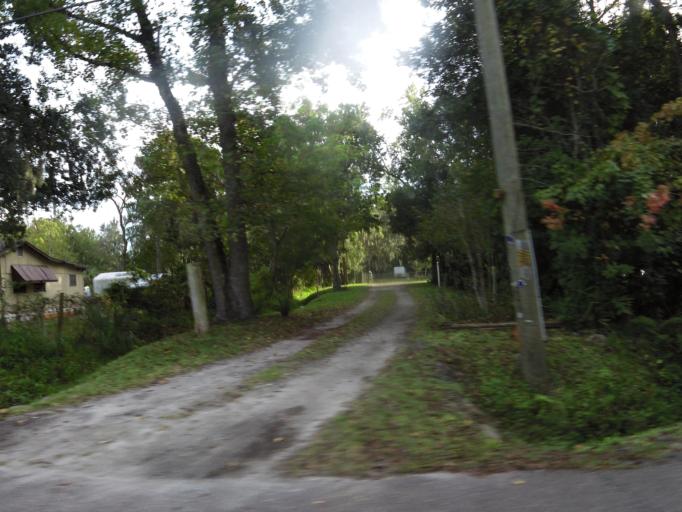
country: US
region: Florida
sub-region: Duval County
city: Jacksonville
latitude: 30.4187
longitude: -81.6526
